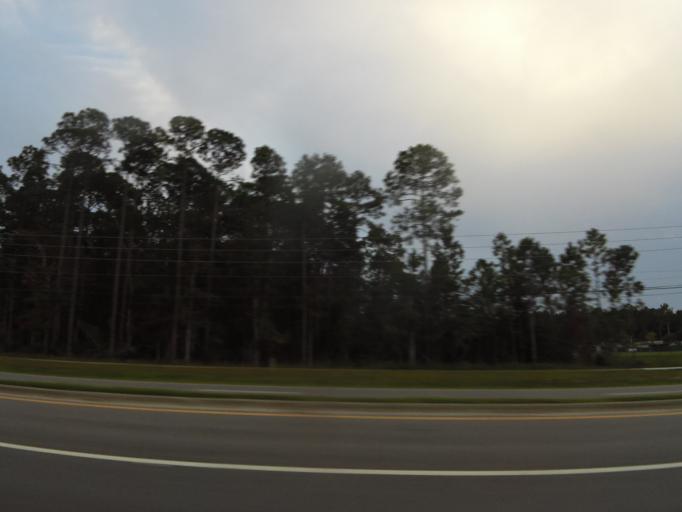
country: US
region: Florida
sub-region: Saint Johns County
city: Fruit Cove
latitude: 30.1063
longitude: -81.5505
